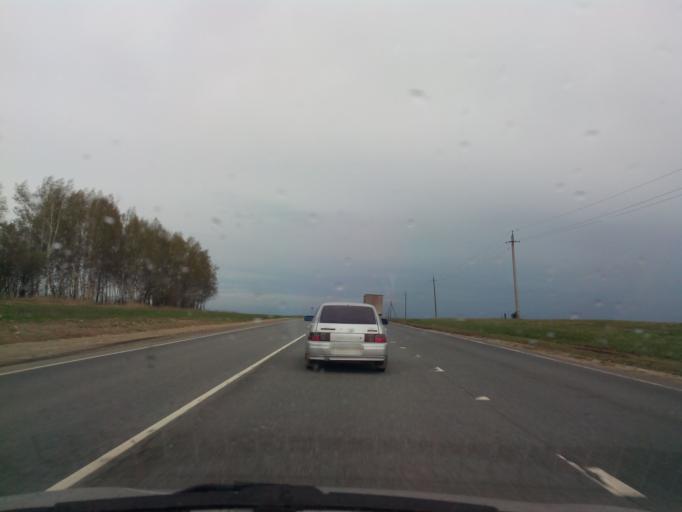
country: RU
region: Moskovskaya
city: Uzunovo
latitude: 54.4940
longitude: 38.5108
